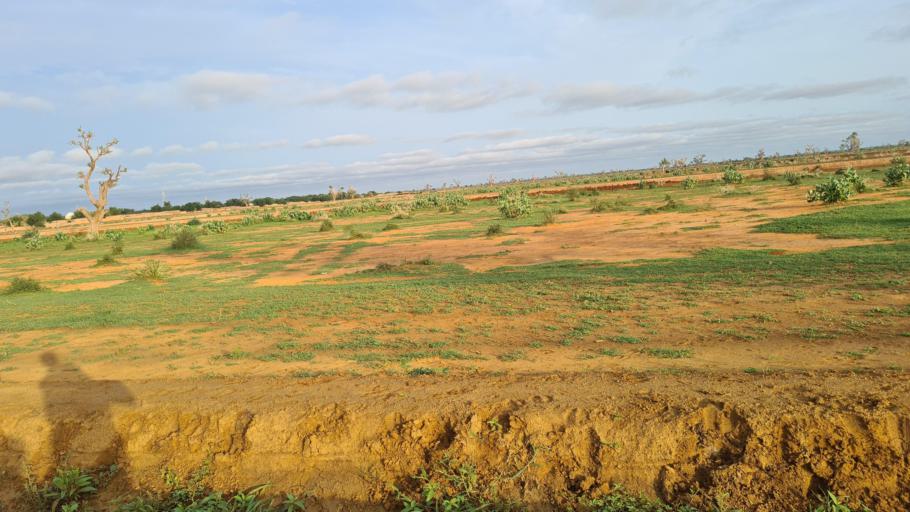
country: NE
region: Tahoua
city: Birni N Konni
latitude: 13.7883
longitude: 5.2344
